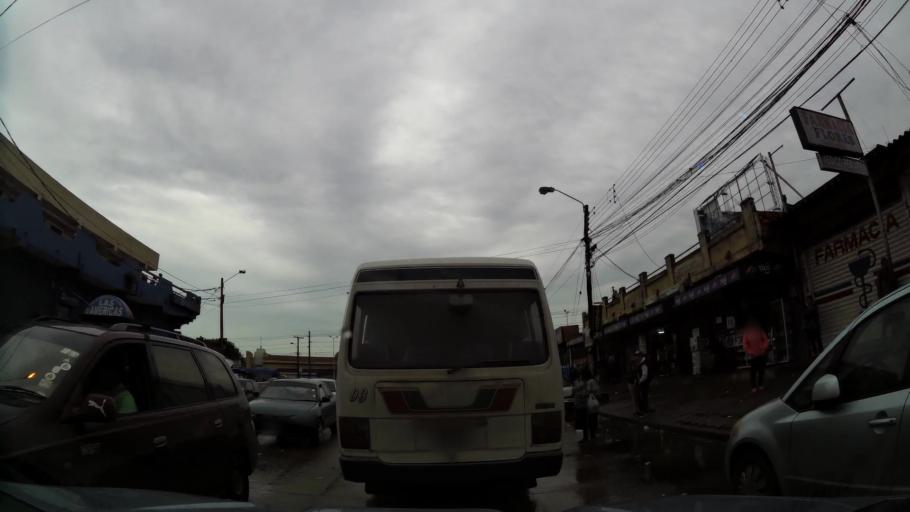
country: BO
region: Santa Cruz
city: Santa Cruz de la Sierra
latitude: -17.8102
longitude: -63.1902
